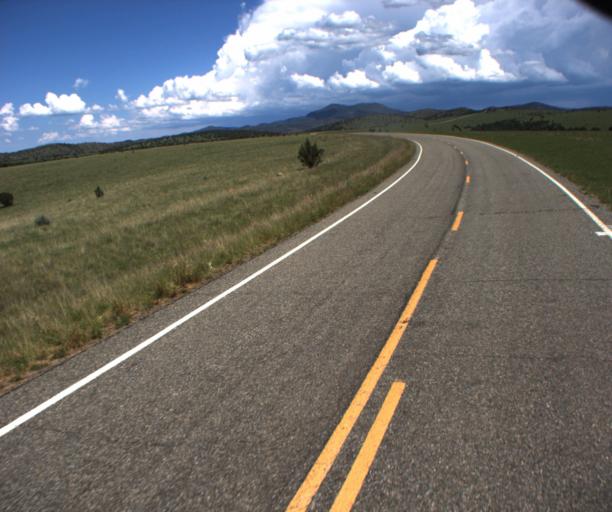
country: US
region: Arizona
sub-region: Greenlee County
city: Morenci
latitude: 33.3153
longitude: -109.3499
